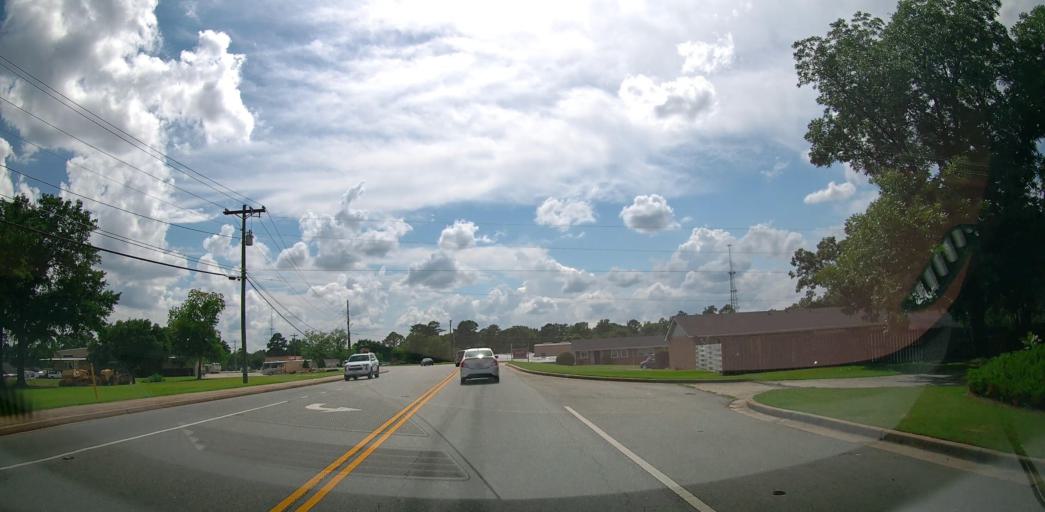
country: US
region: Georgia
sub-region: Houston County
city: Centerville
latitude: 32.6064
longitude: -83.6584
